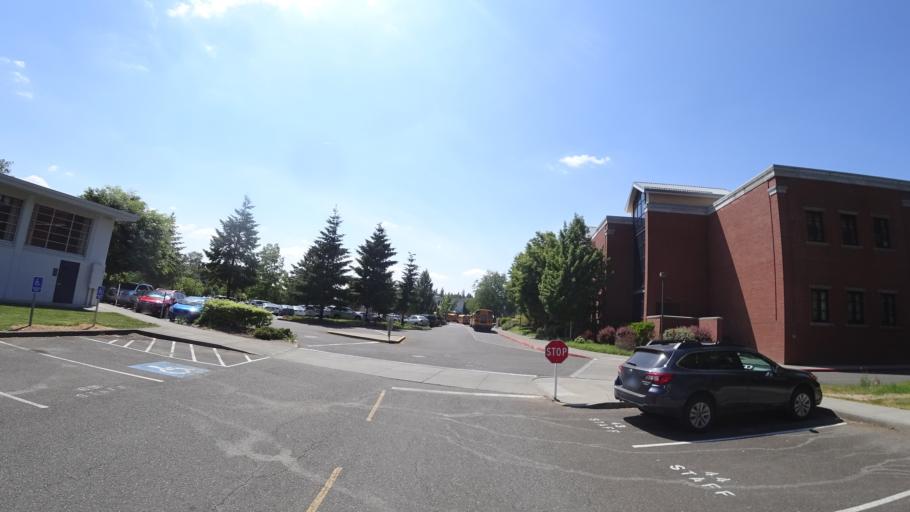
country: US
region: Oregon
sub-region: Clackamas County
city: Lake Oswego
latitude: 45.4269
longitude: -122.7009
